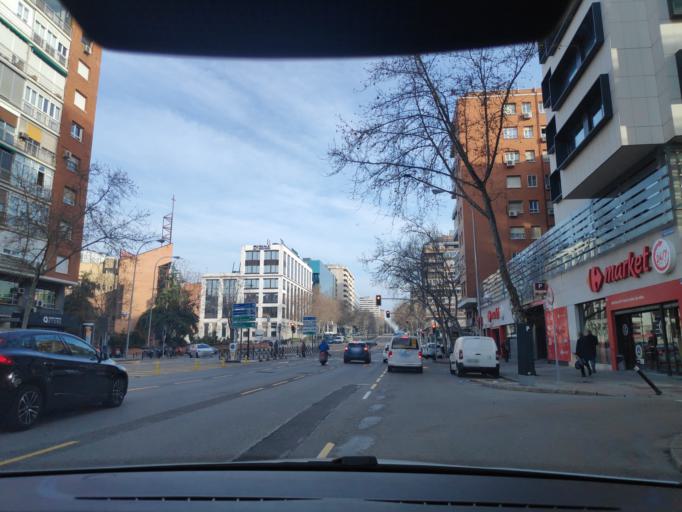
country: ES
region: Madrid
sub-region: Provincia de Madrid
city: Salamanca
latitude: 40.4406
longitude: -3.6786
